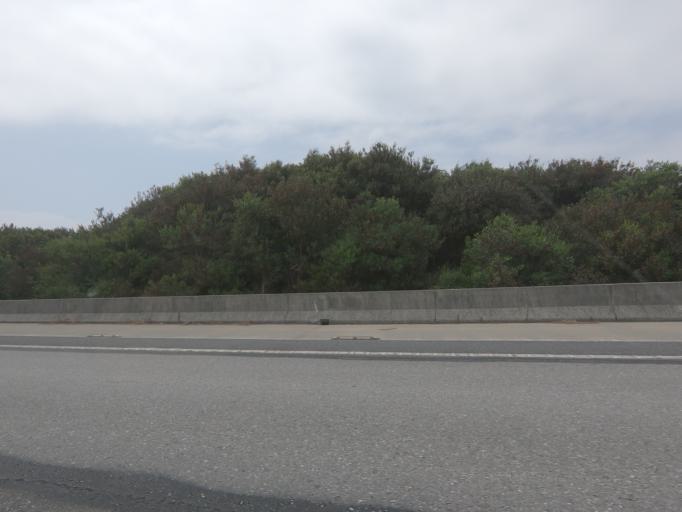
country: ES
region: Galicia
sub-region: Provincia de Pontevedra
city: Oia
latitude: 41.9811
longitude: -8.8846
